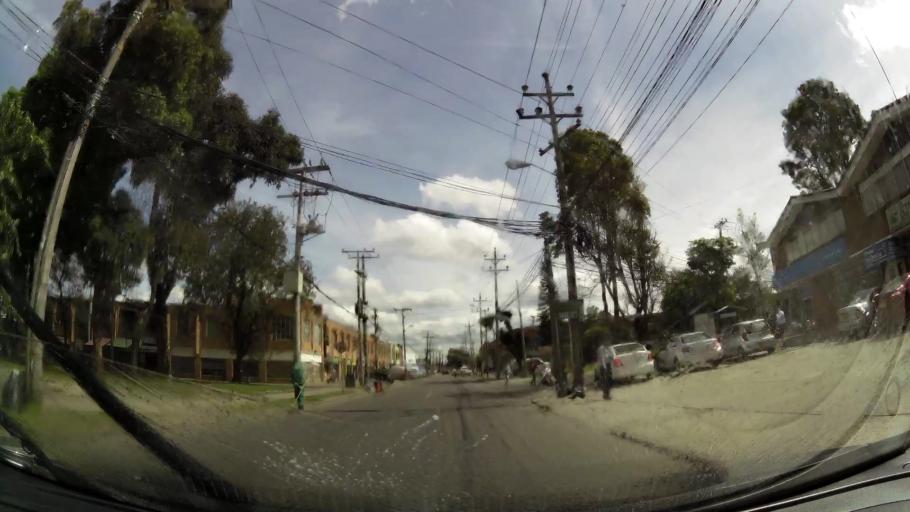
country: CO
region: Bogota D.C.
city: Bogota
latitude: 4.6896
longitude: -74.1175
